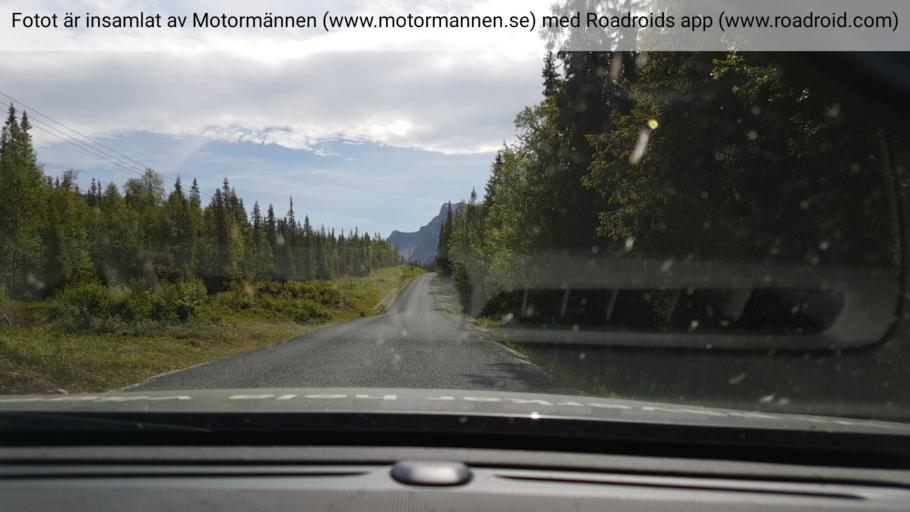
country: SE
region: Vaesterbotten
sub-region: Vilhelmina Kommun
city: Sjoberg
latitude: 65.2675
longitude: 15.3717
